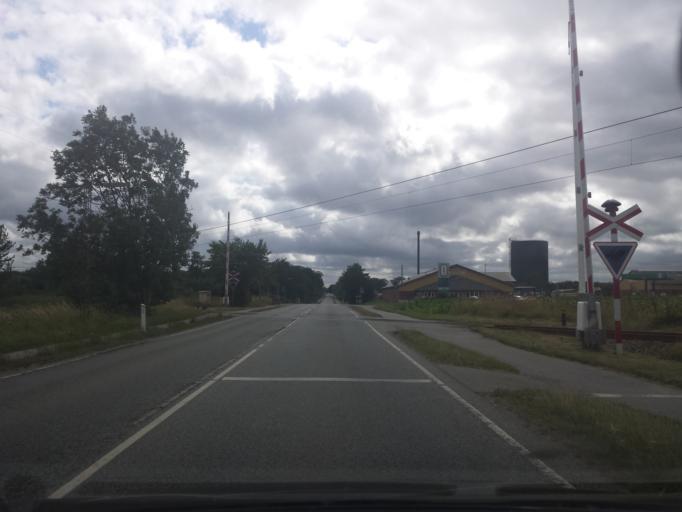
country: DK
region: South Denmark
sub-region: Sonderborg Kommune
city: Grasten
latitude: 54.9334
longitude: 9.6108
